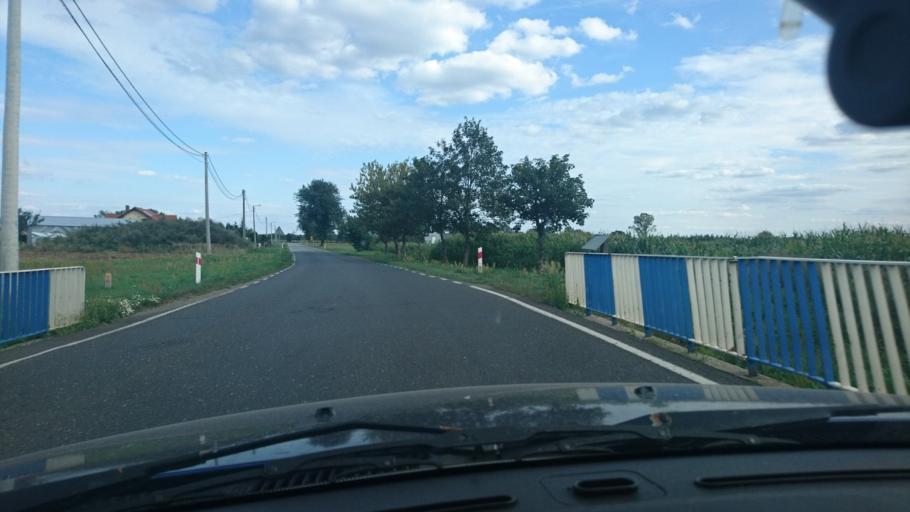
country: PL
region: Greater Poland Voivodeship
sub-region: Powiat ostrowski
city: Odolanow
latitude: 51.5672
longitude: 17.6929
